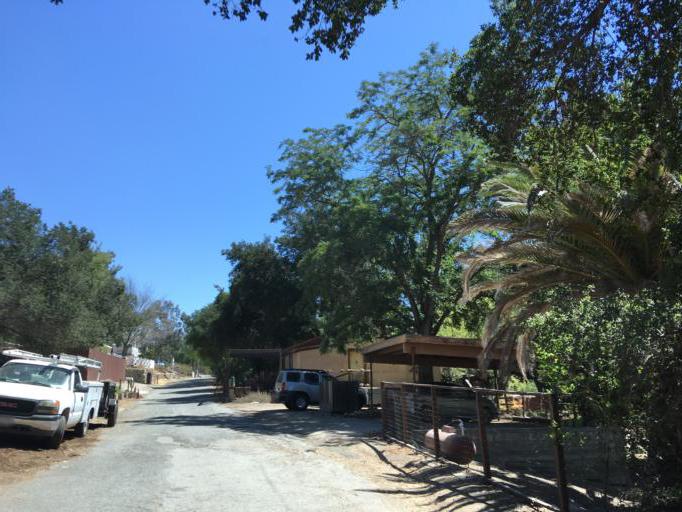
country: US
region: California
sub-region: Los Angeles County
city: Agua Dulce
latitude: 34.5101
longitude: -118.3640
